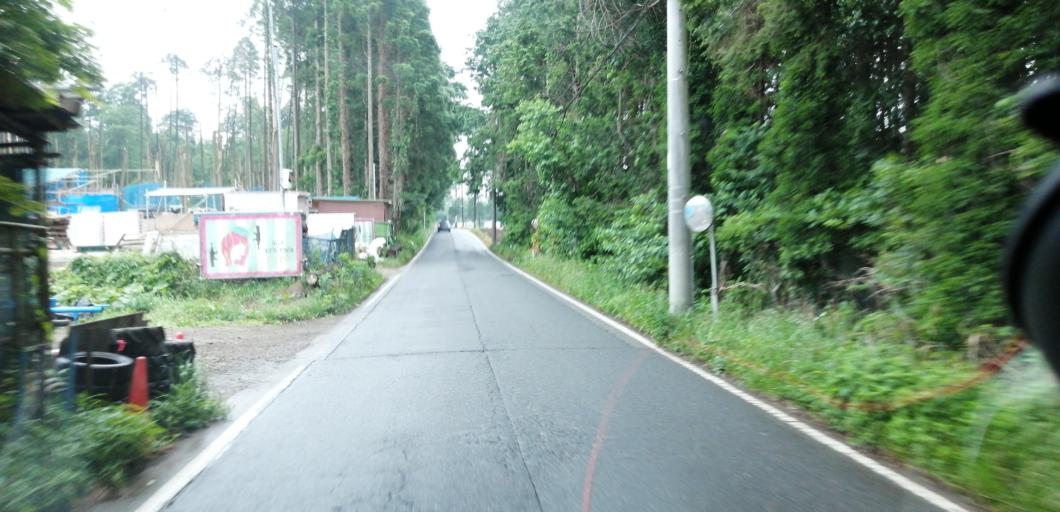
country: JP
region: Chiba
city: Oami
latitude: 35.5666
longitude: 140.2584
